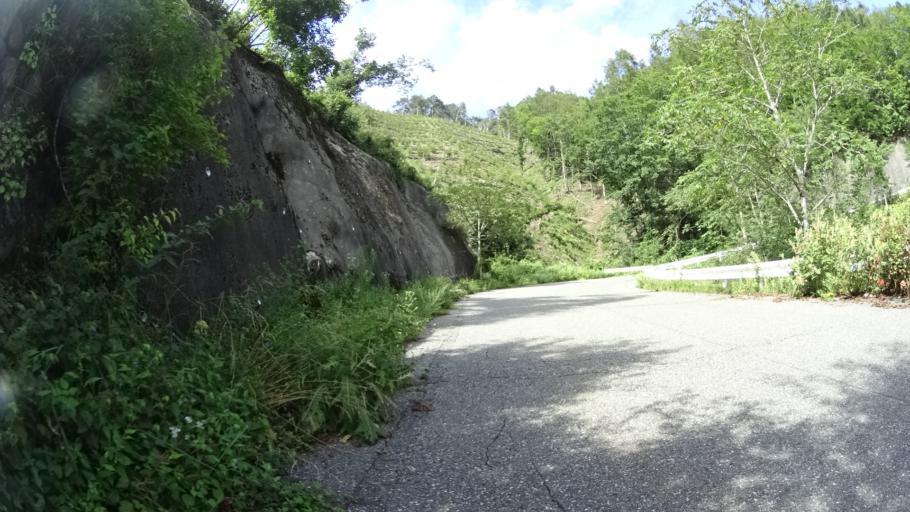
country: JP
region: Yamanashi
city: Nirasaki
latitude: 35.9118
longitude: 138.5406
